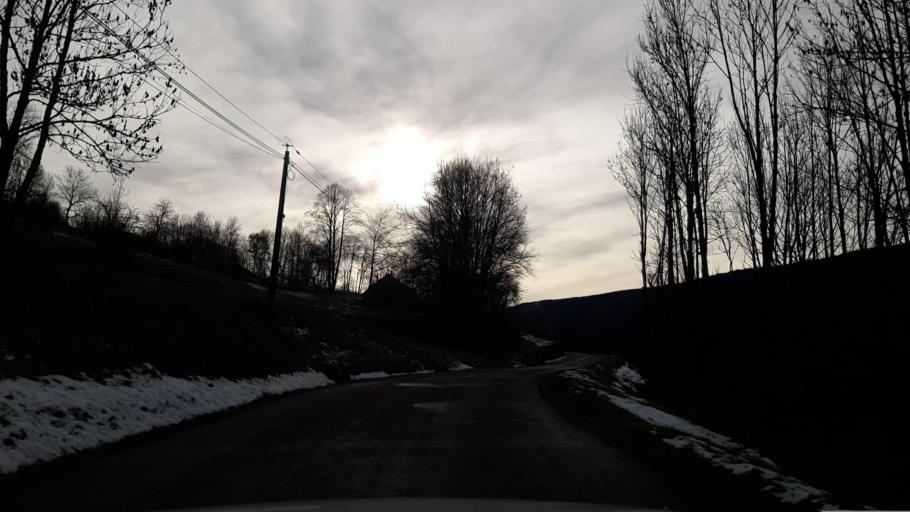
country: FR
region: Rhone-Alpes
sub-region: Departement de la Haute-Savoie
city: Cusy
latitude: 45.6622
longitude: 6.0965
